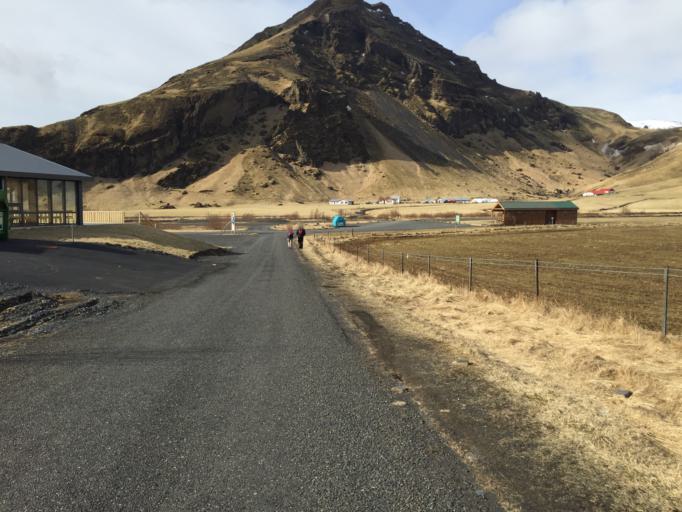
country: IS
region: South
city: Vestmannaeyjar
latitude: 63.5273
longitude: -19.5104
